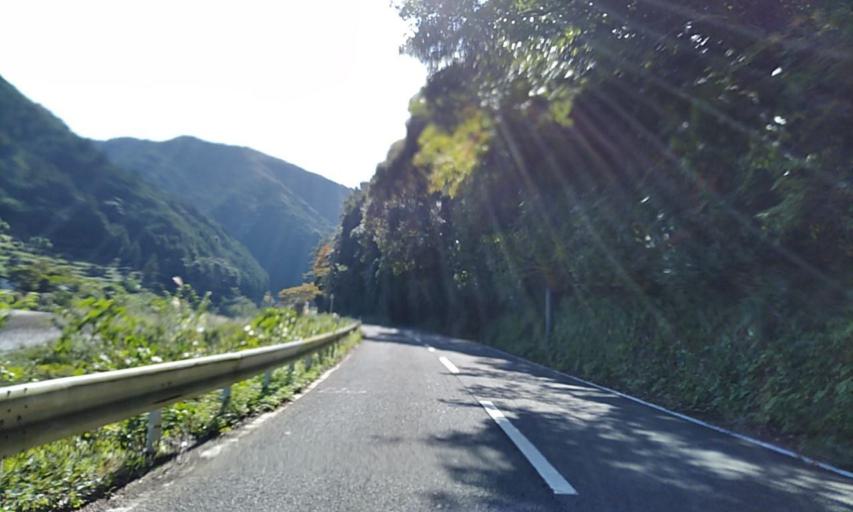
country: JP
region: Wakayama
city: Kainan
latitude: 34.0673
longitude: 135.3562
